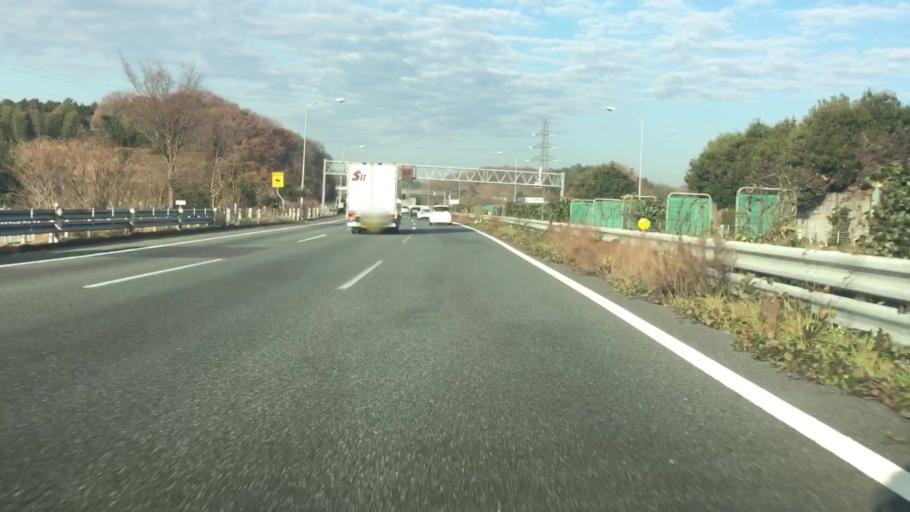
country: JP
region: Saitama
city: Ogawa
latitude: 36.0663
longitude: 139.3198
